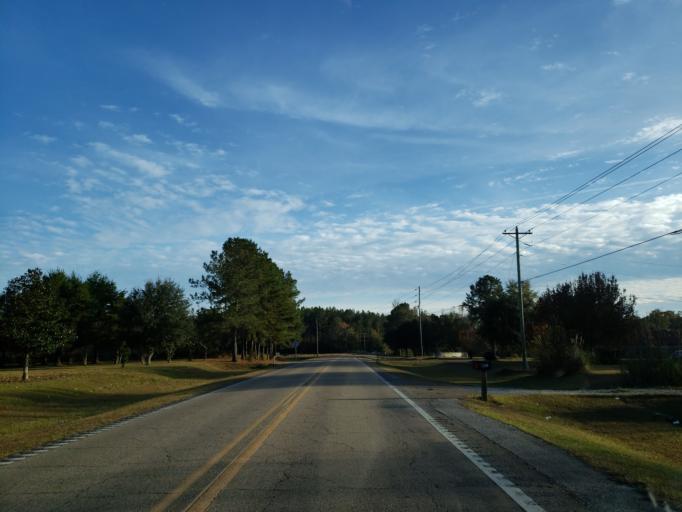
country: US
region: Mississippi
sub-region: Lamar County
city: West Hattiesburg
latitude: 31.2802
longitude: -89.4665
